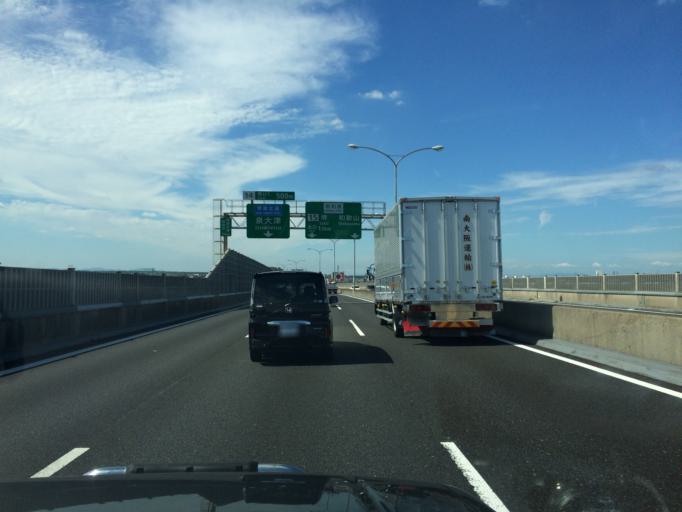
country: JP
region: Osaka
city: Takaishi
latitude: 34.5232
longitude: 135.4978
